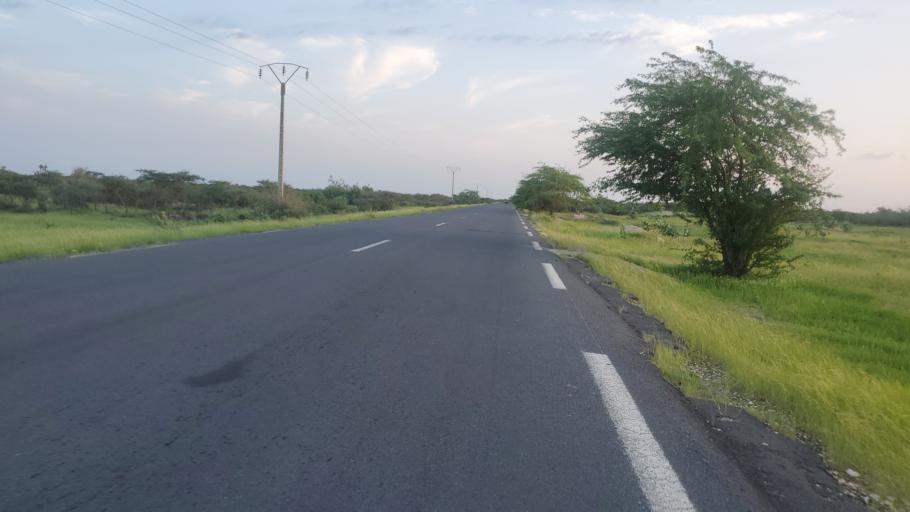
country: SN
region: Saint-Louis
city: Saint-Louis
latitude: 16.1278
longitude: -16.4131
